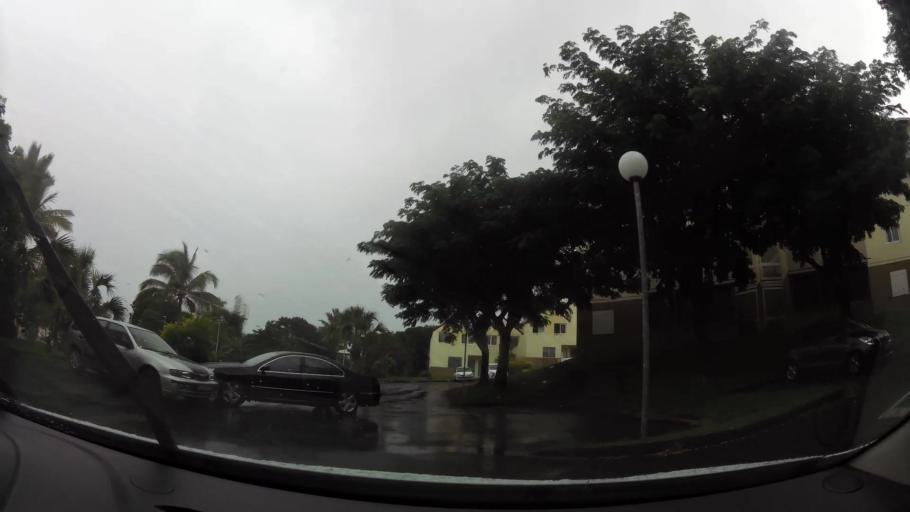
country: RE
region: Reunion
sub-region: Reunion
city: Saint-Andre
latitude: -20.9640
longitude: 55.6460
